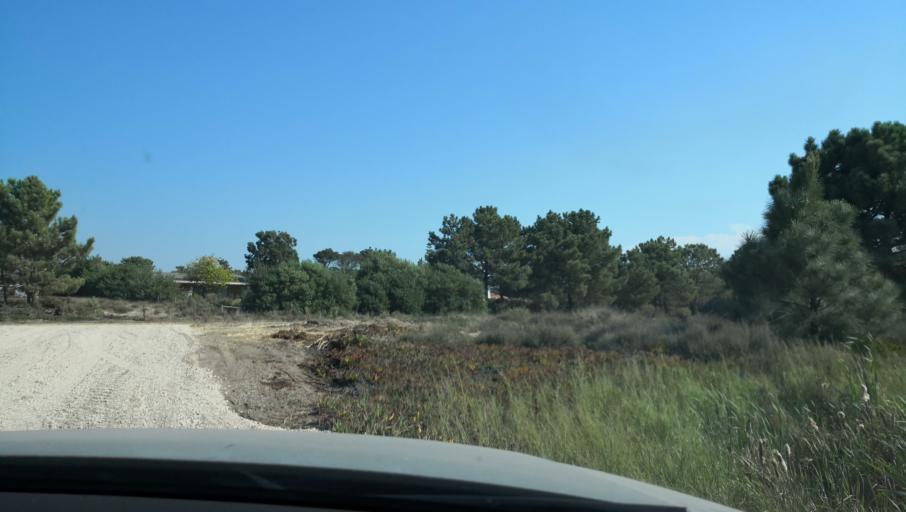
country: PT
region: Setubal
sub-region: Setubal
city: Setubal
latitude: 38.3931
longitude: -8.7888
